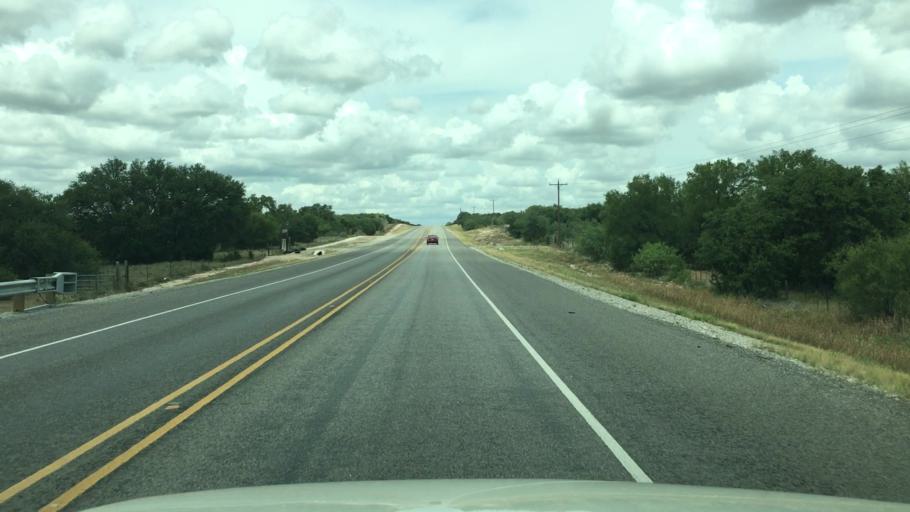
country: US
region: Texas
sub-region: McCulloch County
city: Brady
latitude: 31.0406
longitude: -99.2418
